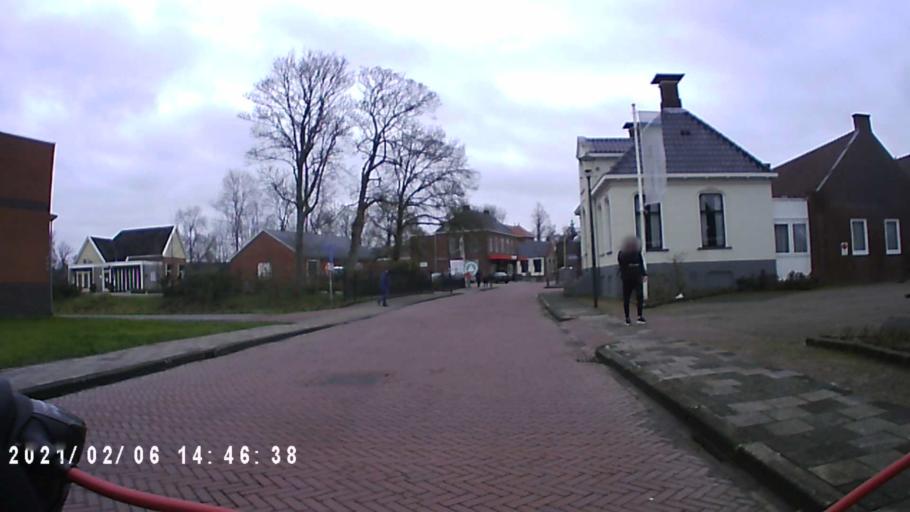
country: NL
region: Groningen
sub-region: Gemeente Winsum
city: Winsum
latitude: 53.3928
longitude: 6.5582
